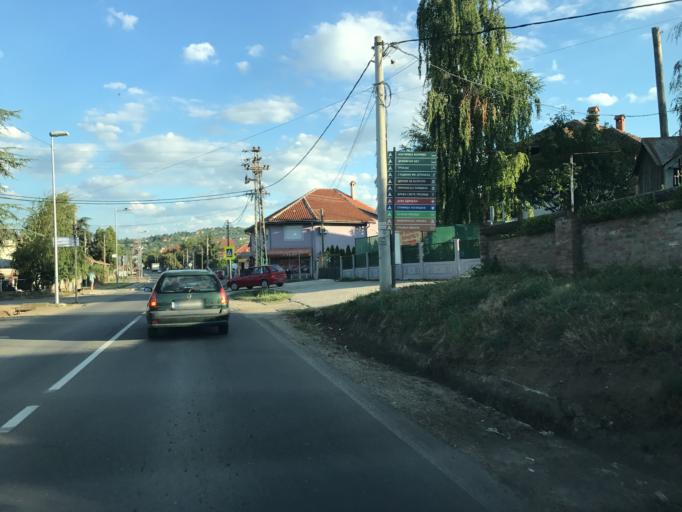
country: RS
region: Central Serbia
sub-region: Belgrade
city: Grocka
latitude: 44.6786
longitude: 20.7125
